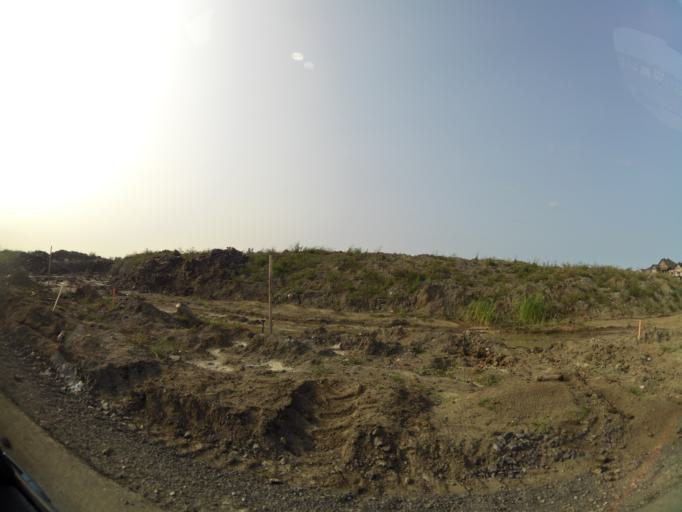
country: CA
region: Ontario
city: Ottawa
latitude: 45.4442
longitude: -75.4853
